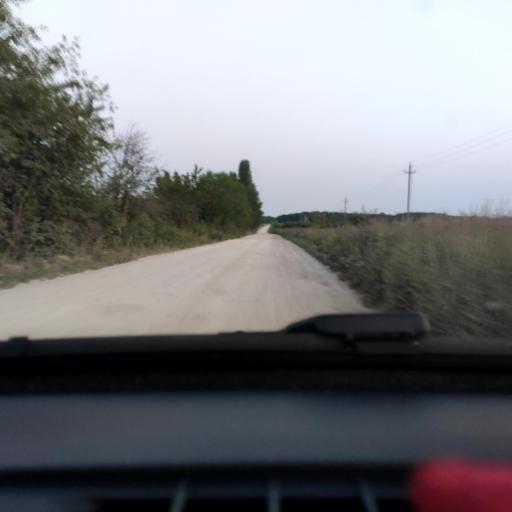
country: RU
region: Voronezj
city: Podgornoye
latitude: 51.8631
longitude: 39.0998
